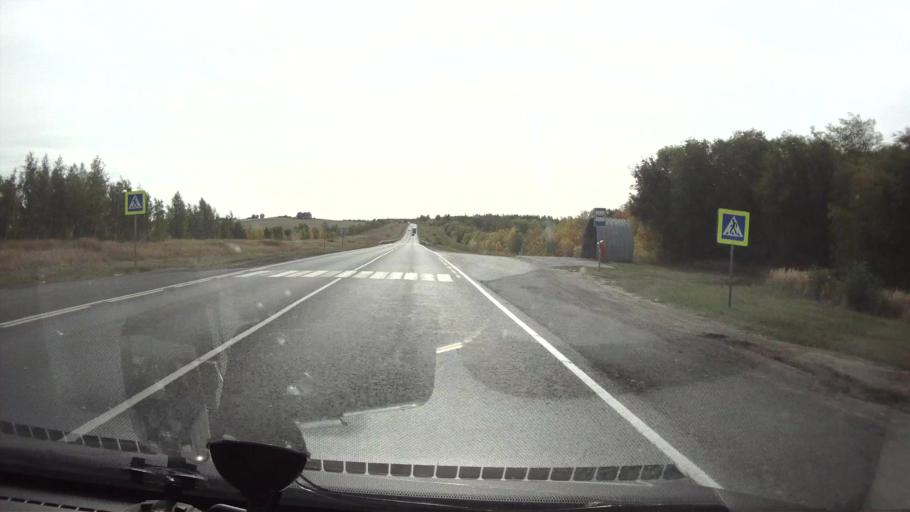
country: RU
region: Saratov
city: Balakovo
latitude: 52.1766
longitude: 47.8369
